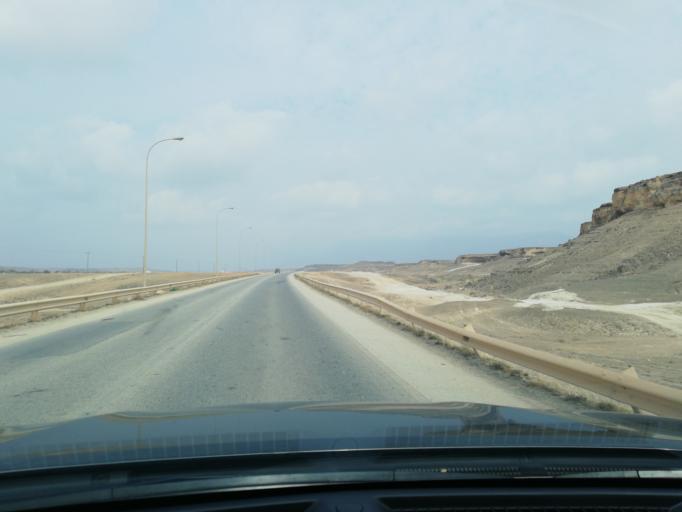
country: OM
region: Zufar
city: Salalah
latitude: 16.9538
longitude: 53.9197
